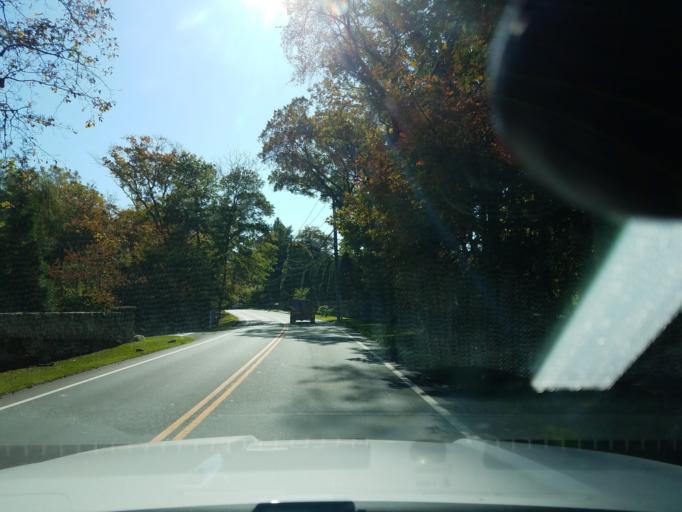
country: US
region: Connecticut
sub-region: Fairfield County
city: Glenville
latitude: 41.0891
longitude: -73.6304
